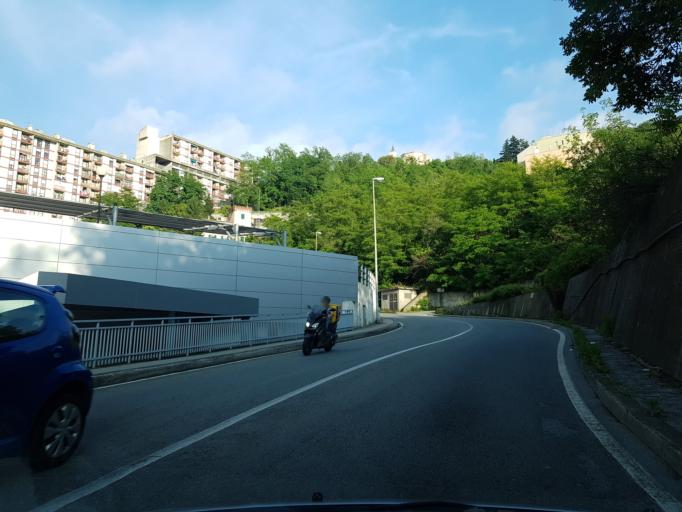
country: IT
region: Liguria
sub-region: Provincia di Genova
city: Genoa
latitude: 44.4518
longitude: 8.9037
